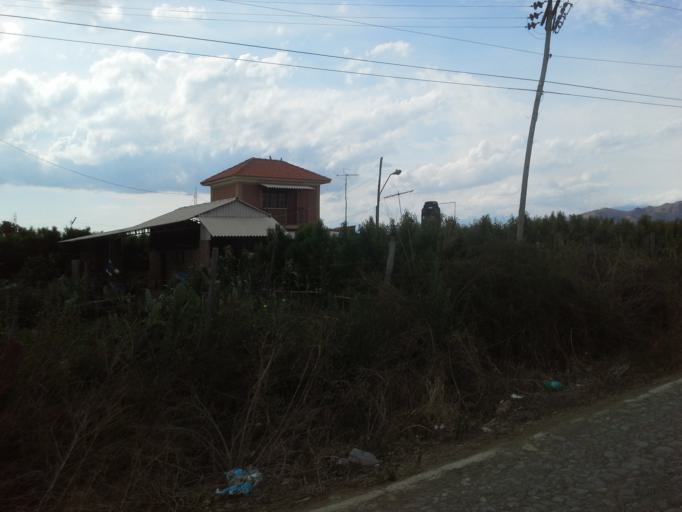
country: BO
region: Cochabamba
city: Tarata
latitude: -17.5888
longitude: -66.0185
